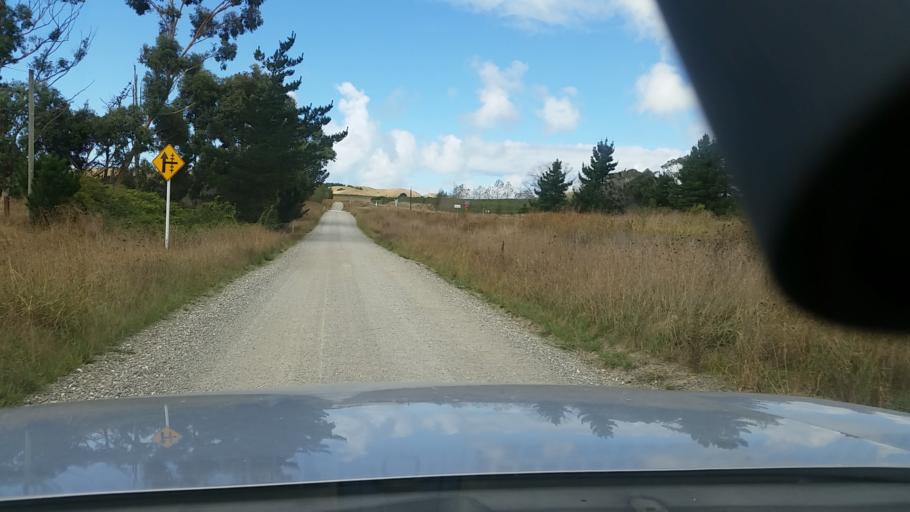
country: NZ
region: Marlborough
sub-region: Marlborough District
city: Blenheim
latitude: -41.6861
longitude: 174.1294
